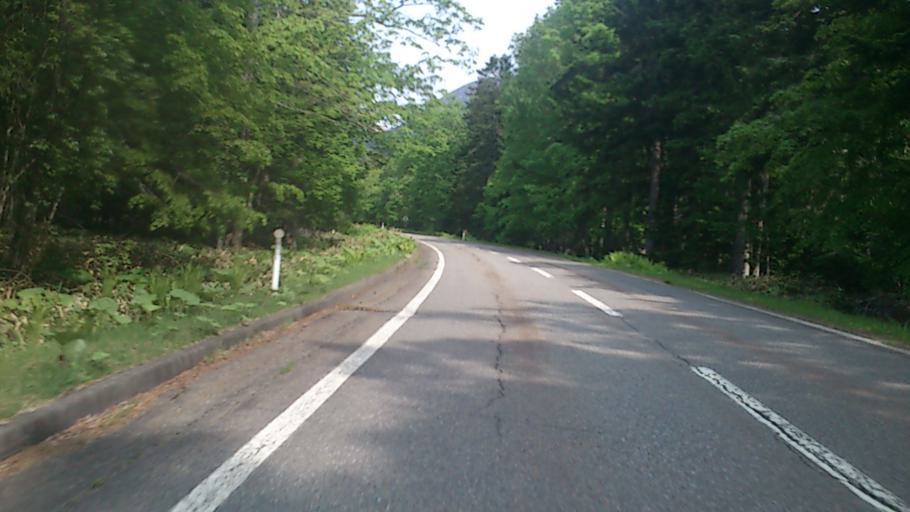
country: JP
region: Hokkaido
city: Kitami
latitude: 43.4027
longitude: 143.9668
